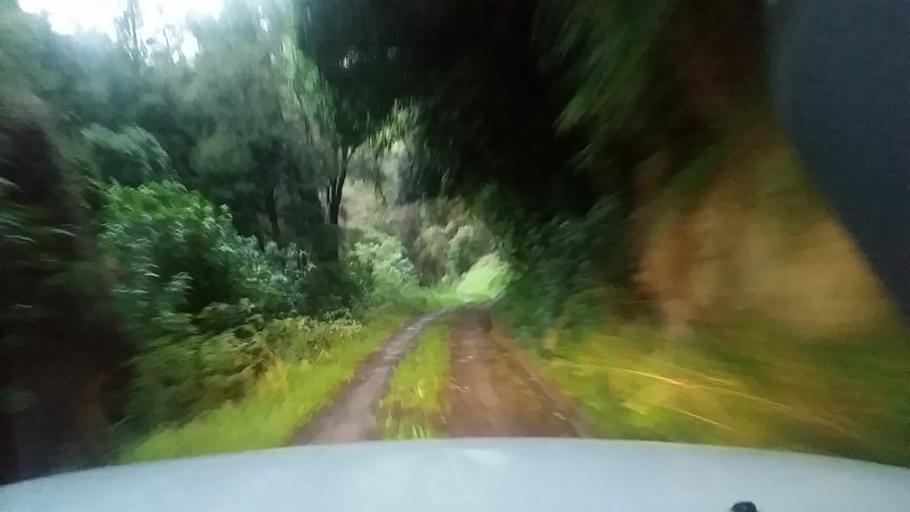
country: NZ
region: Canterbury
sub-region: Christchurch City
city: Christchurch
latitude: -43.7871
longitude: 172.8847
